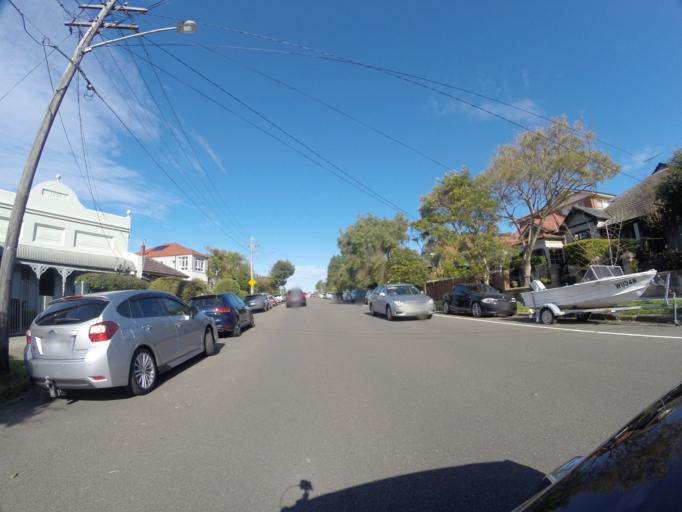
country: AU
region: New South Wales
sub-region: Randwick
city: Clovelly
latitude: -33.9071
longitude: 151.2544
